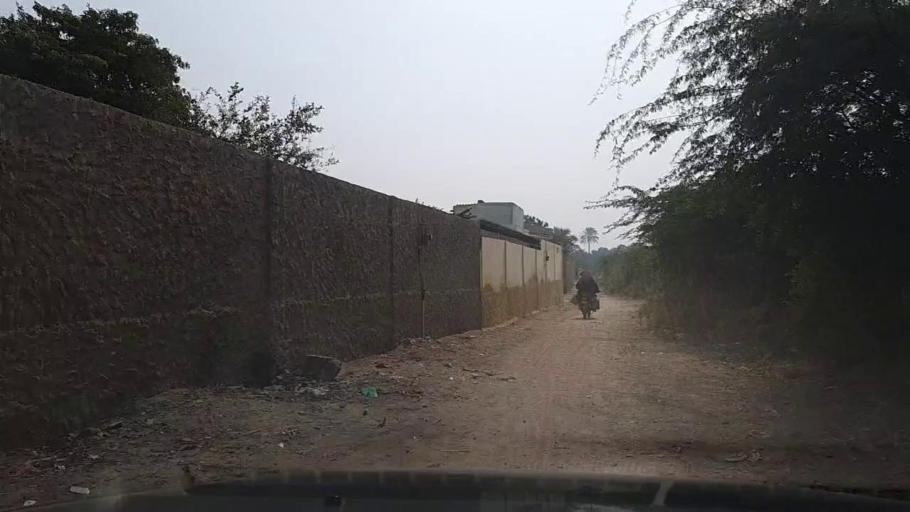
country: PK
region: Sindh
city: Thatta
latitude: 24.5546
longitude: 67.8390
